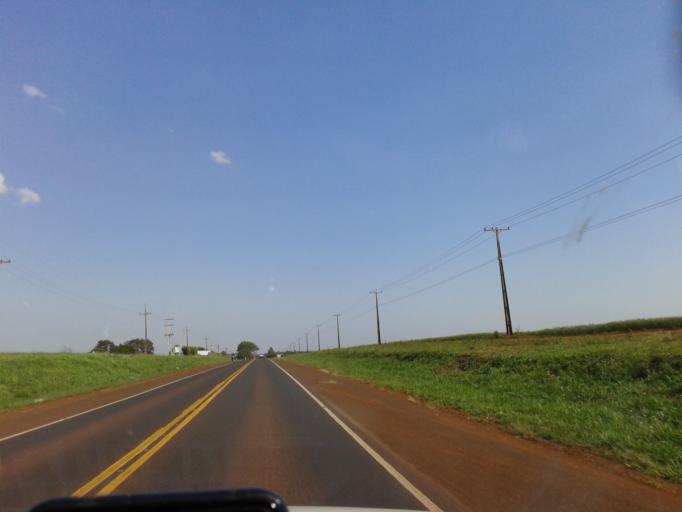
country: PY
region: Alto Parana
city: Santa Rita
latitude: -25.6984
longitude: -55.0187
